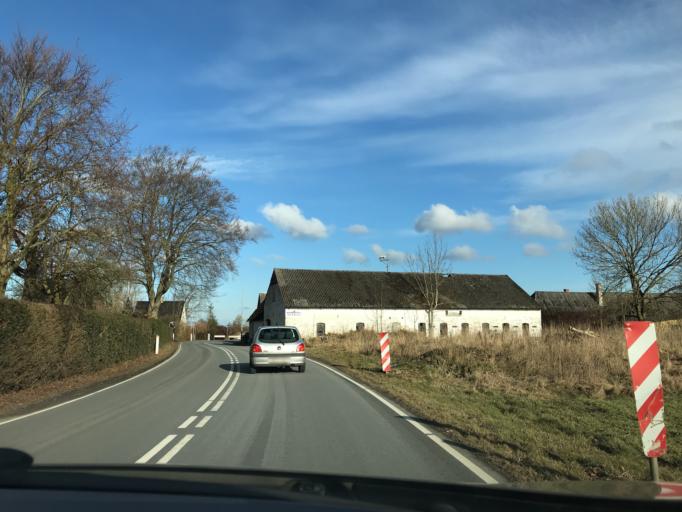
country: DK
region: South Denmark
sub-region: Nordfyns Kommune
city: Bogense
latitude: 55.5238
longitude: 10.0750
